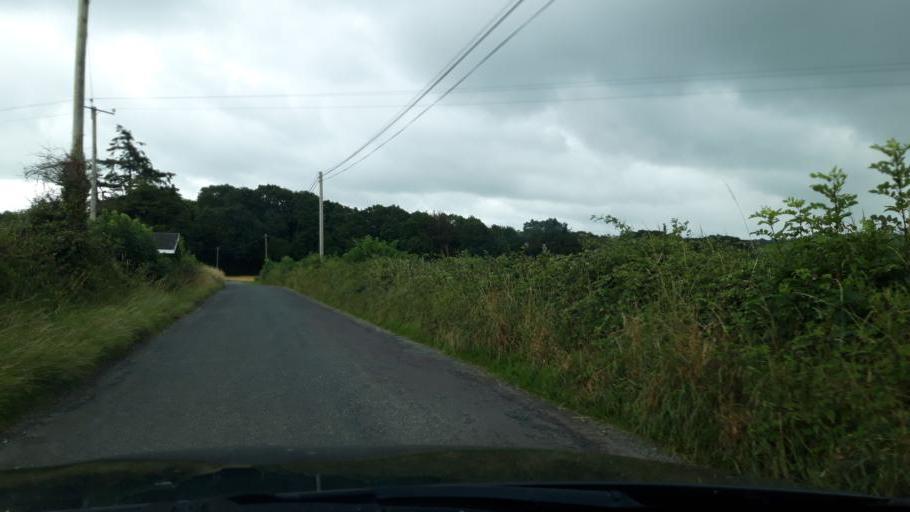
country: IE
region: Munster
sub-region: County Cork
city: Youghal
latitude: 52.1274
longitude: -7.9742
